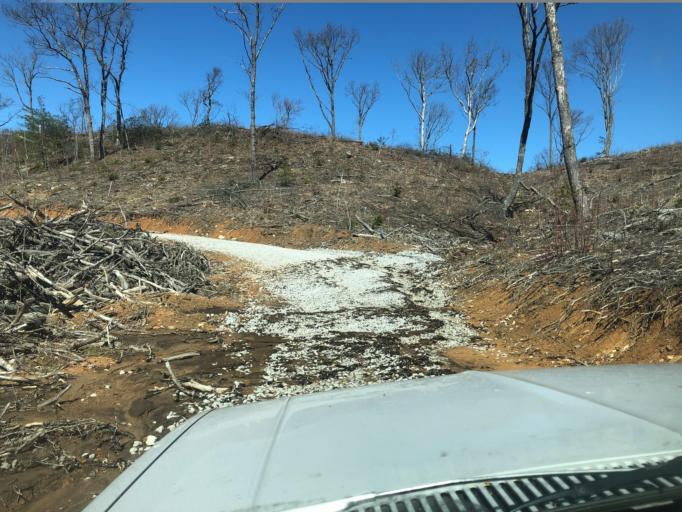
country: US
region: Tennessee
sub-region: Cumberland County
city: Fairfield Glade
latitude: 35.9705
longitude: -84.7629
